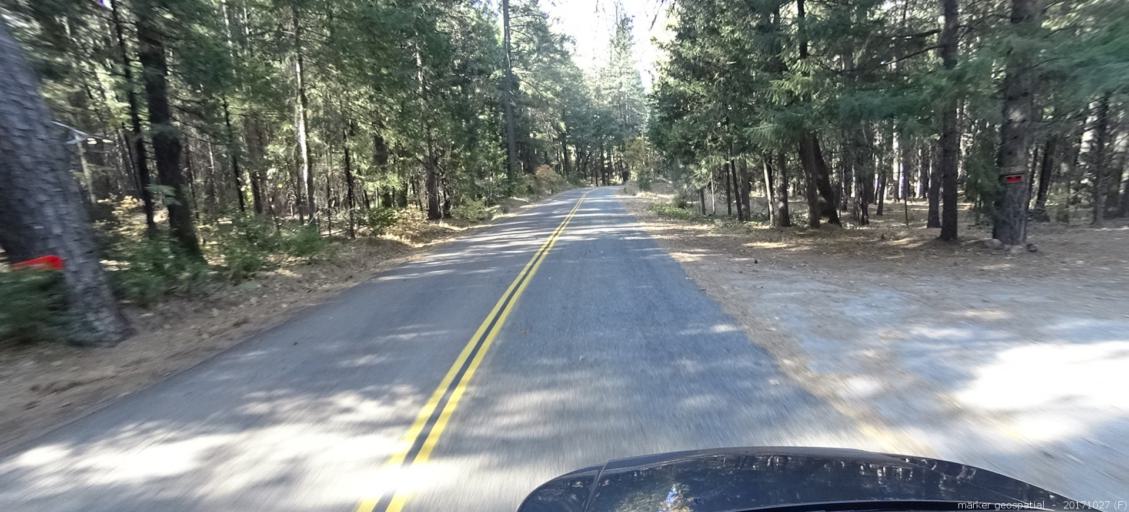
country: US
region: California
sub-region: Shasta County
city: Burney
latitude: 40.8202
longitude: -121.9616
